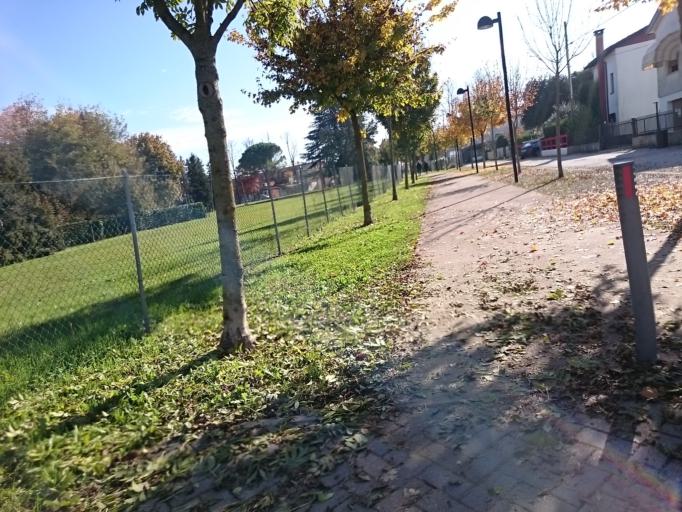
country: IT
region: Veneto
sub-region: Provincia di Padova
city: Piazzola sul Brenta
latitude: 45.5435
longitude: 11.7782
